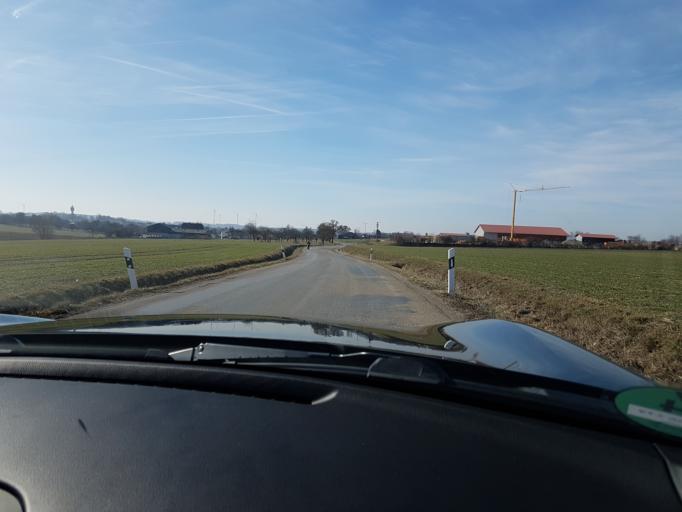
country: DE
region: Baden-Wuerttemberg
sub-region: Regierungsbezirk Stuttgart
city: Langenburg
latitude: 49.2607
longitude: 9.8771
